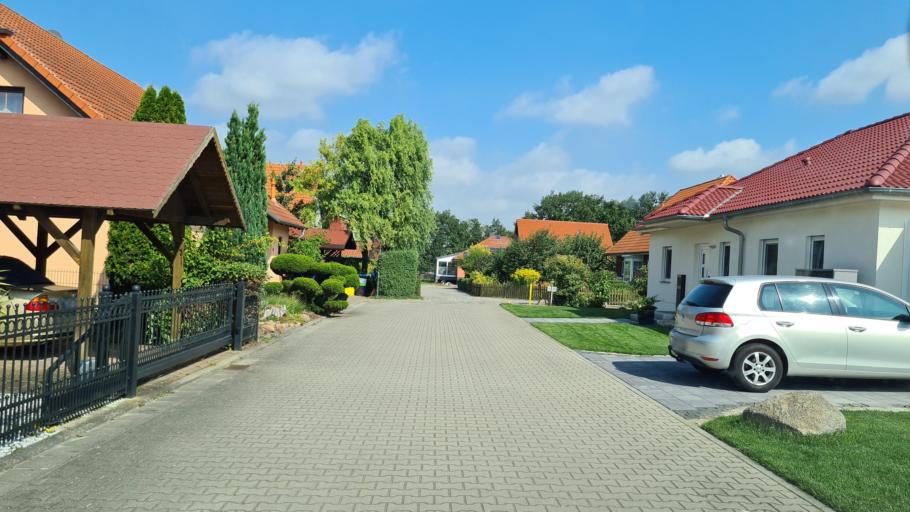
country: DE
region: Brandenburg
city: Luckau
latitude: 51.8553
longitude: 13.6925
